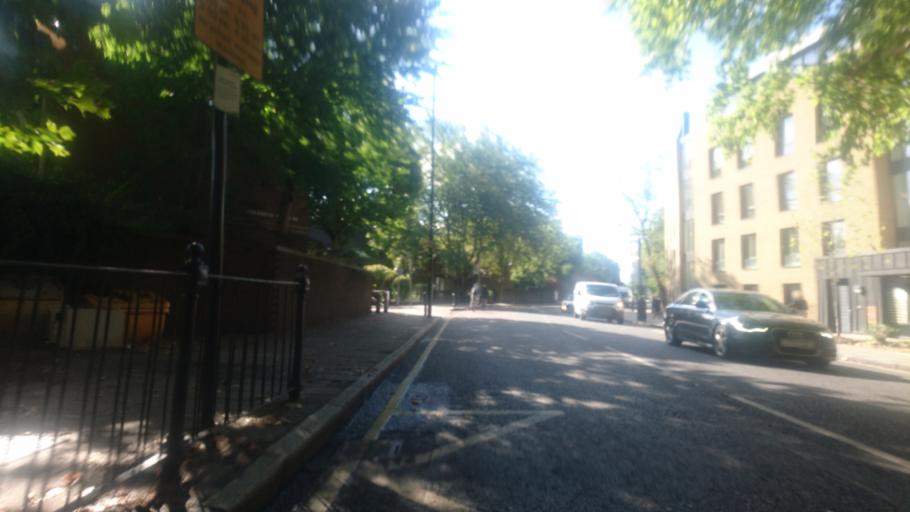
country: GB
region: England
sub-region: Greater London
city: Islington
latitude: 51.5447
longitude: -0.1015
